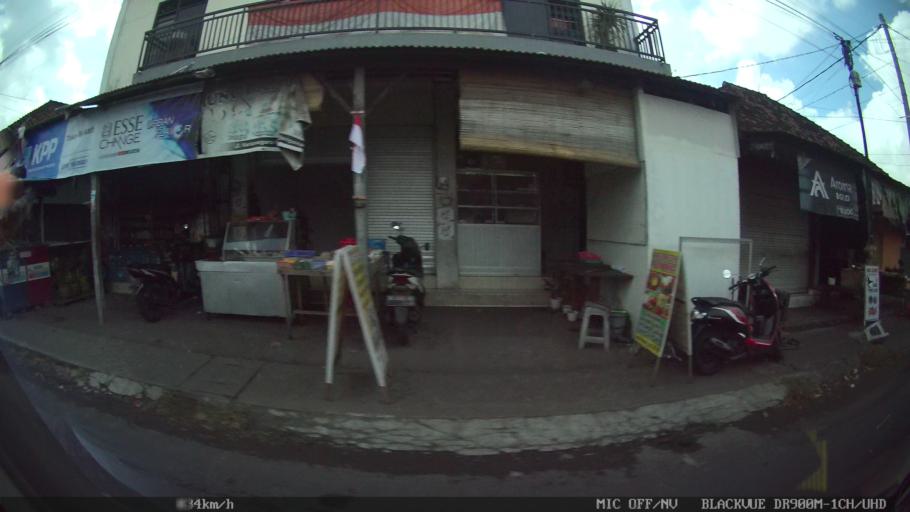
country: ID
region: Bali
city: Banjar Kertasari
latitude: -8.6220
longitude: 115.2026
